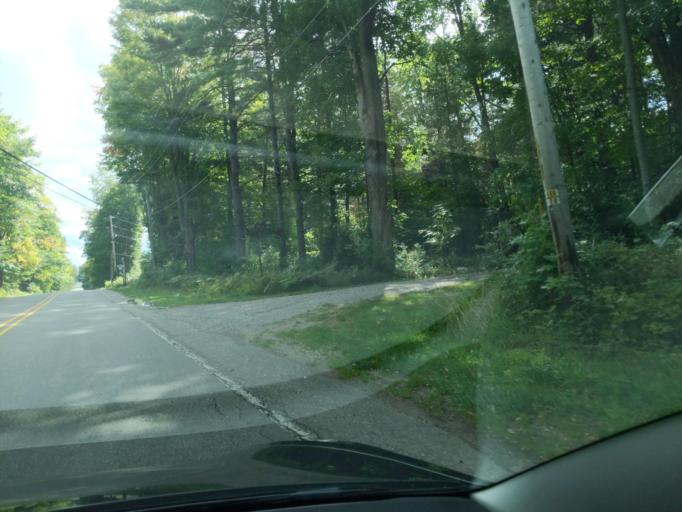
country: US
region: Michigan
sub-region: Antrim County
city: Bellaire
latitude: 44.9287
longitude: -85.2858
